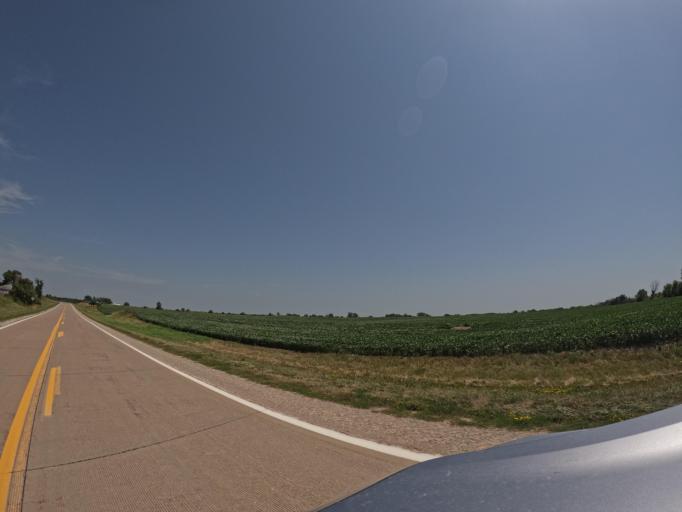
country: US
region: Iowa
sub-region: Henry County
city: Mount Pleasant
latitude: 40.9817
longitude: -91.6259
